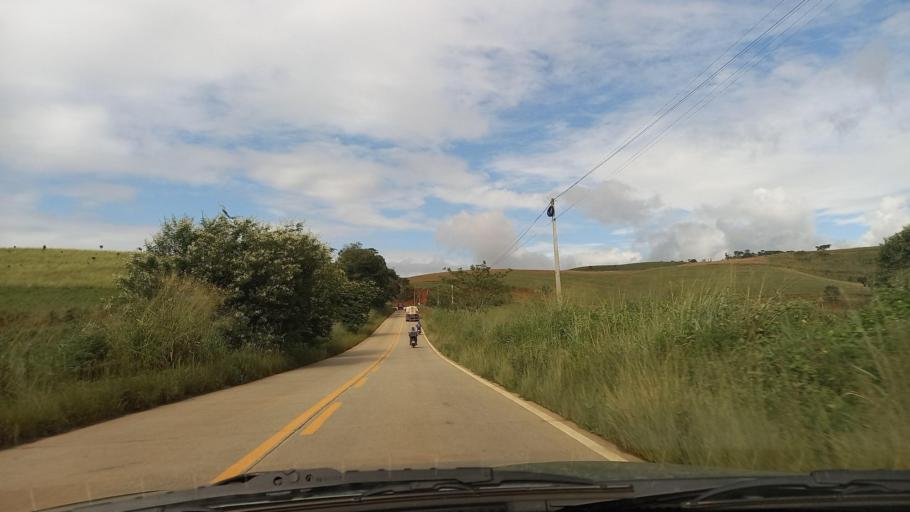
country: BR
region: Pernambuco
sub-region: Maraial
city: Maraial
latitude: -8.7494
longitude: -35.8114
